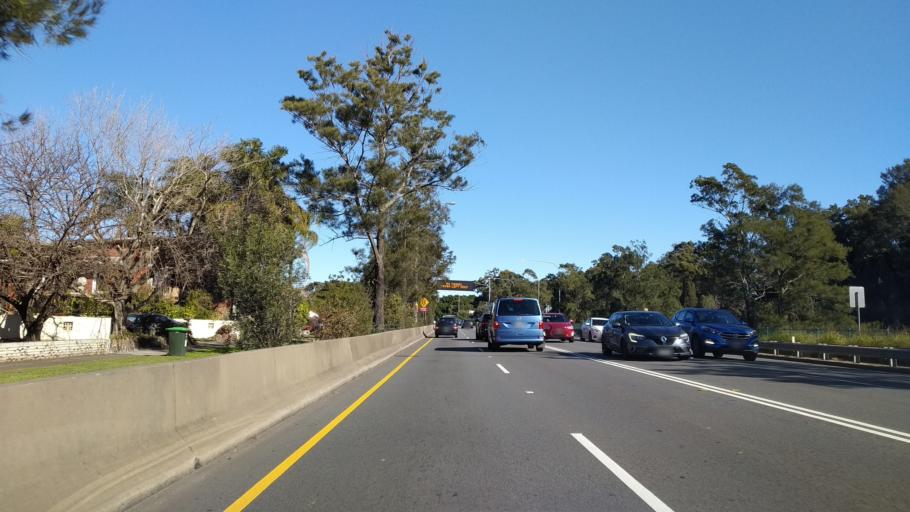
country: AU
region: New South Wales
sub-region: Canada Bay
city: Wareemba
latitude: -33.8716
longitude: 151.1403
